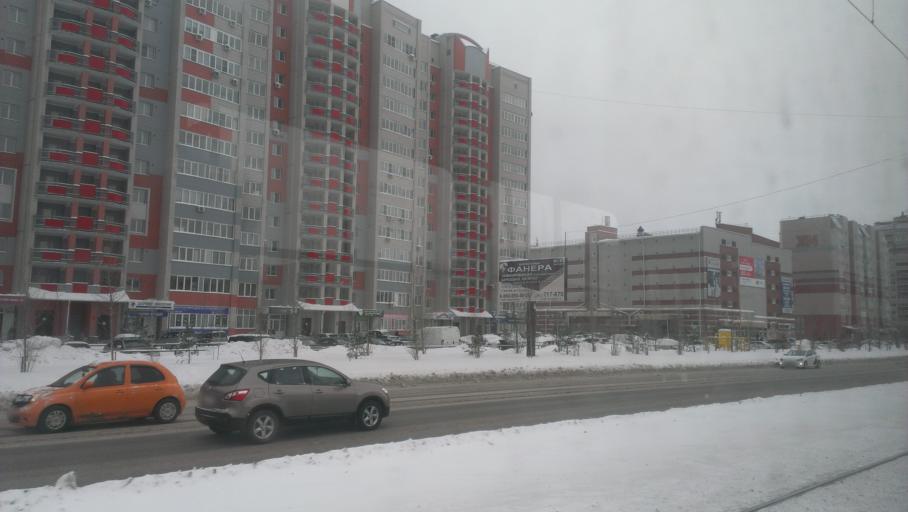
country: RU
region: Altai Krai
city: Novosilikatnyy
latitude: 53.3286
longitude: 83.6798
